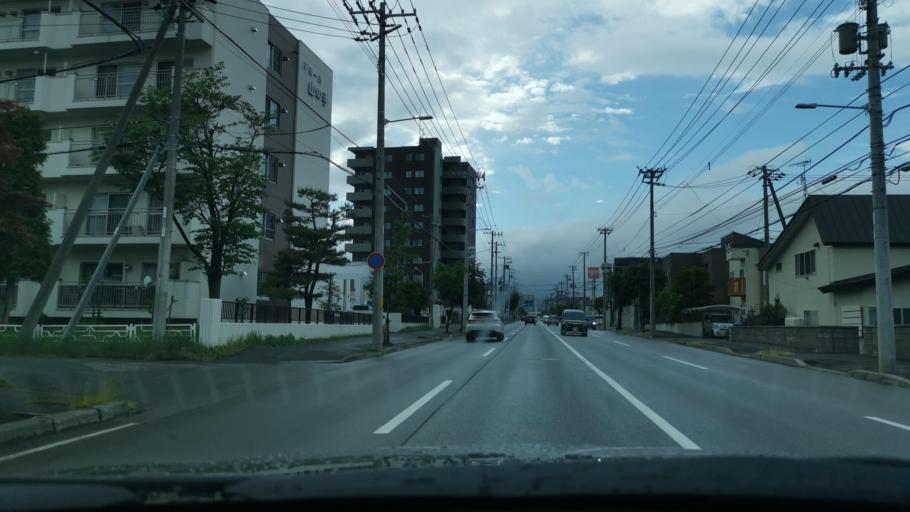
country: JP
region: Hokkaido
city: Sapporo
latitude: 43.0664
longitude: 141.2974
